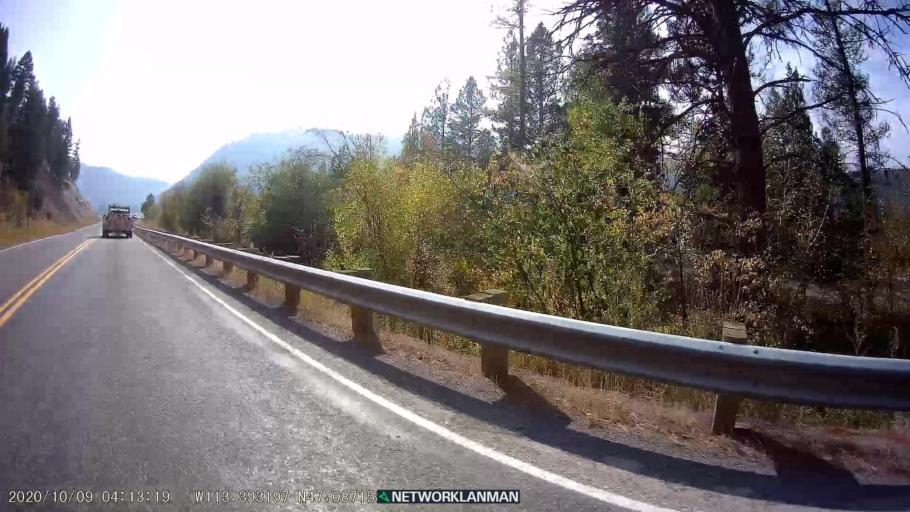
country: US
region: Montana
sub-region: Missoula County
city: Seeley Lake
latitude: 47.0872
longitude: -113.3926
